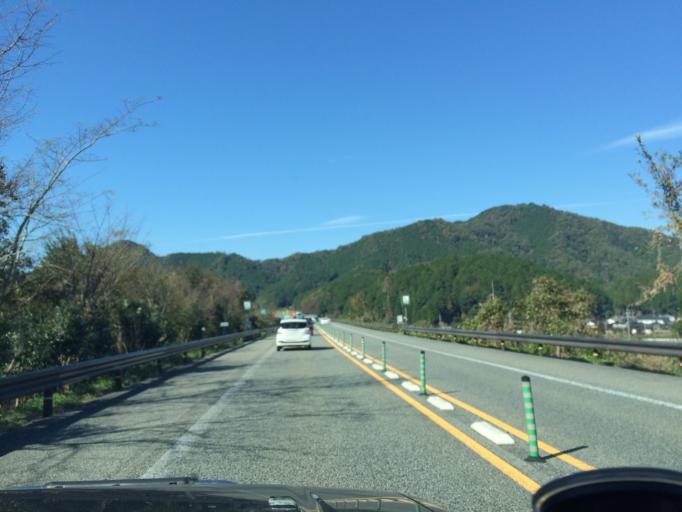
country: JP
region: Kyoto
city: Fukuchiyama
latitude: 35.3074
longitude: 134.8782
